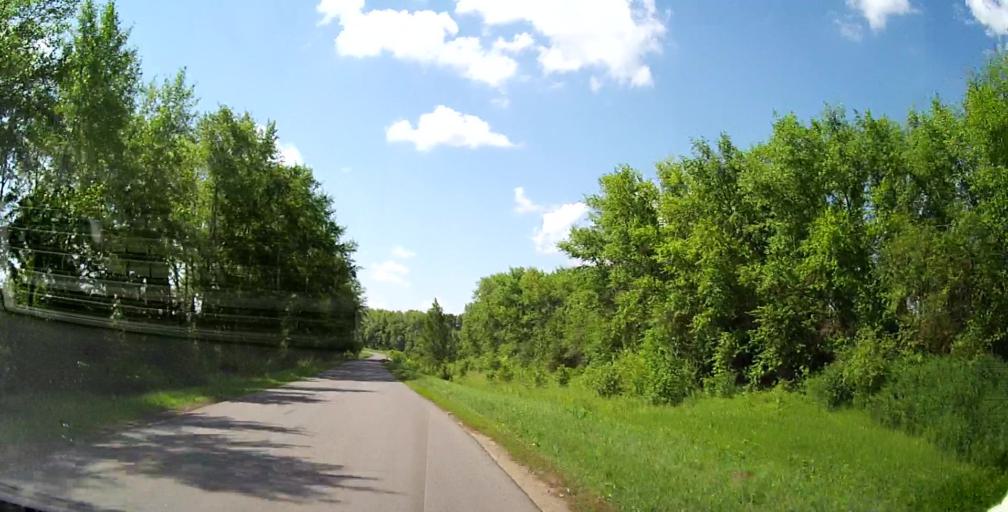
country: RU
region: Lipetsk
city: Chaplygin
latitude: 53.3069
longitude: 39.9532
